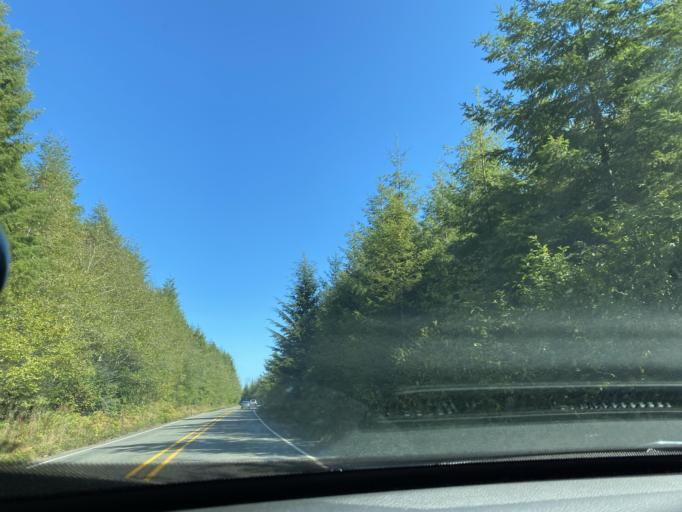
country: US
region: Washington
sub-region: Clallam County
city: Forks
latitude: 47.9335
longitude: -124.4767
